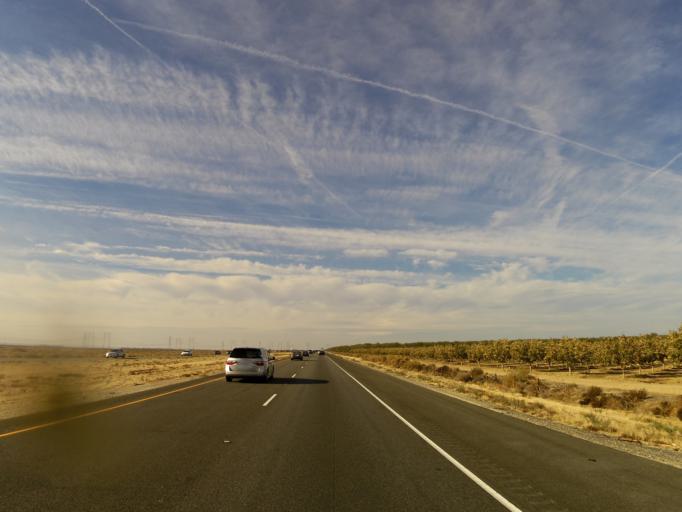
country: US
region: California
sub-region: Kern County
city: Buttonwillow
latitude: 35.4764
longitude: -119.5035
